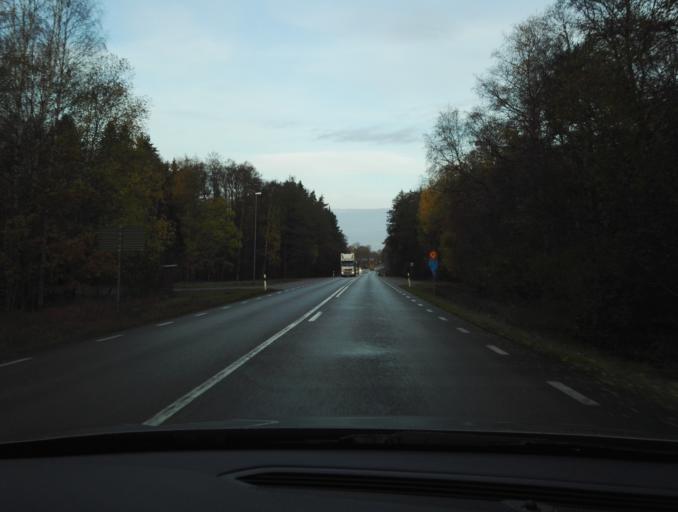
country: SE
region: Kronoberg
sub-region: Alvesta Kommun
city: Moheda
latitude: 56.9918
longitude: 14.6829
